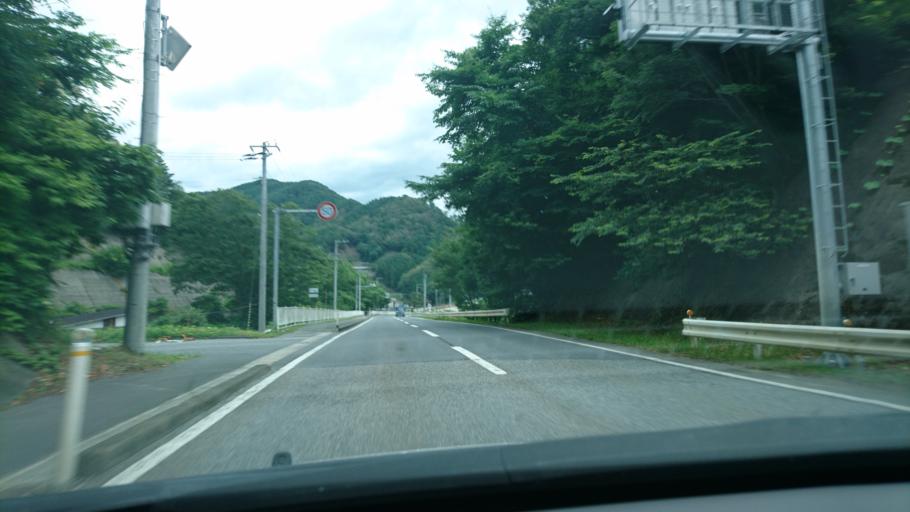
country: JP
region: Iwate
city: Kamaishi
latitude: 39.1994
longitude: 141.8611
